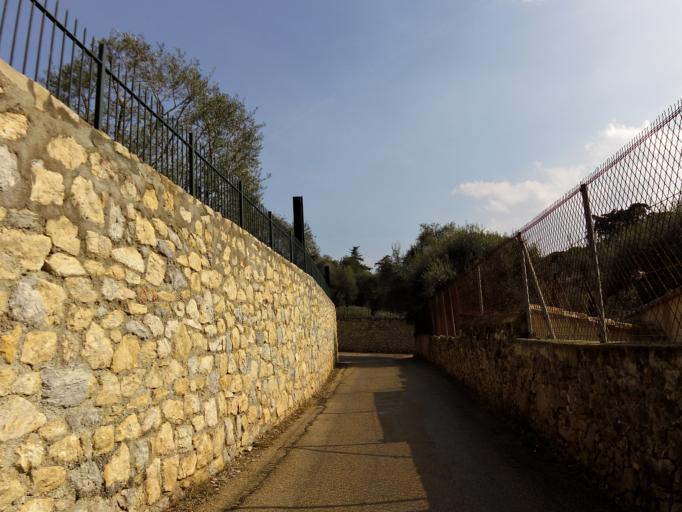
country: FR
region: Provence-Alpes-Cote d'Azur
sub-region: Departement des Alpes-Maritimes
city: Antibes
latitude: 43.5474
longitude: 7.1326
